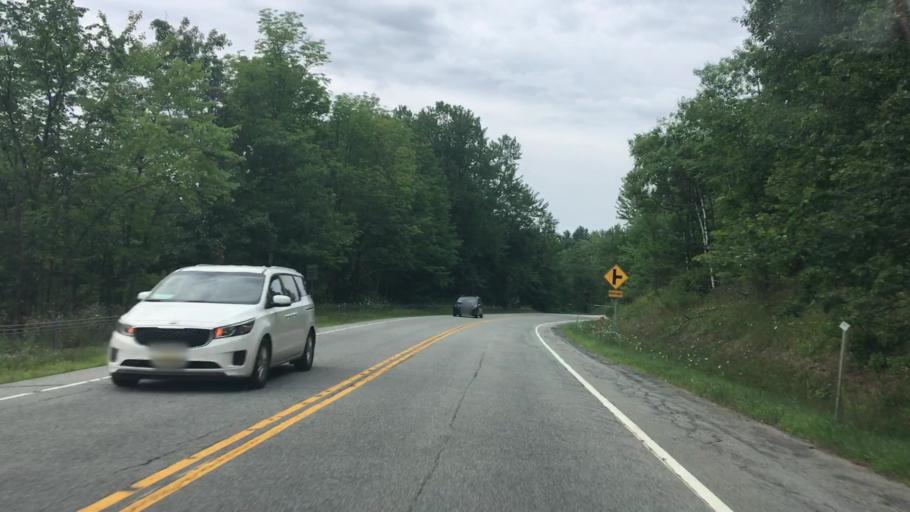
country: US
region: New York
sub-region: Essex County
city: Lake Placid
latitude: 44.2773
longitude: -73.7899
